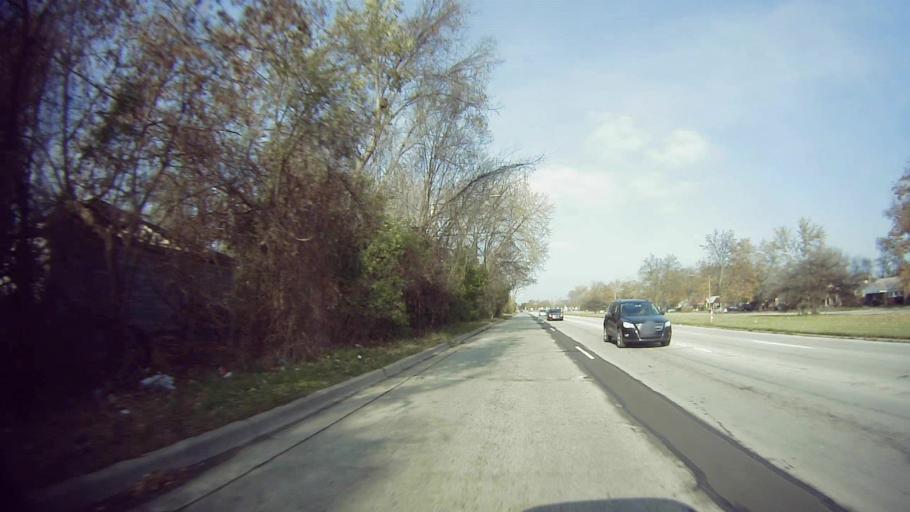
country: US
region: Michigan
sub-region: Wayne County
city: Redford
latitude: 42.4313
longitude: -83.2781
